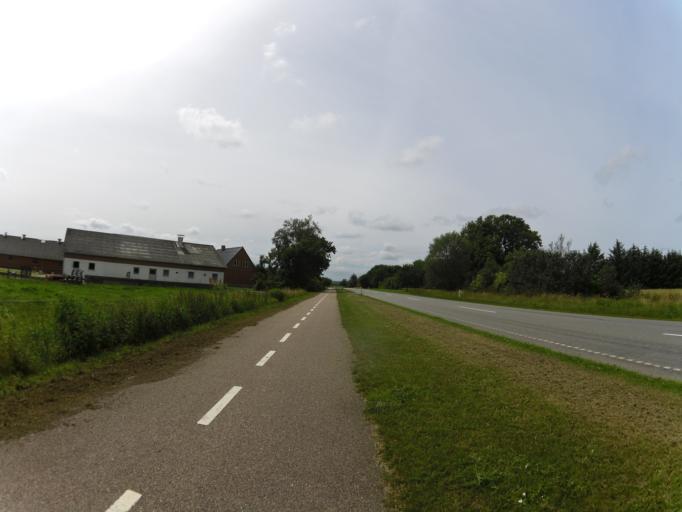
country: DK
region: North Denmark
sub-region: Bronderslev Kommune
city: Dronninglund
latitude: 57.2631
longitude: 10.3284
